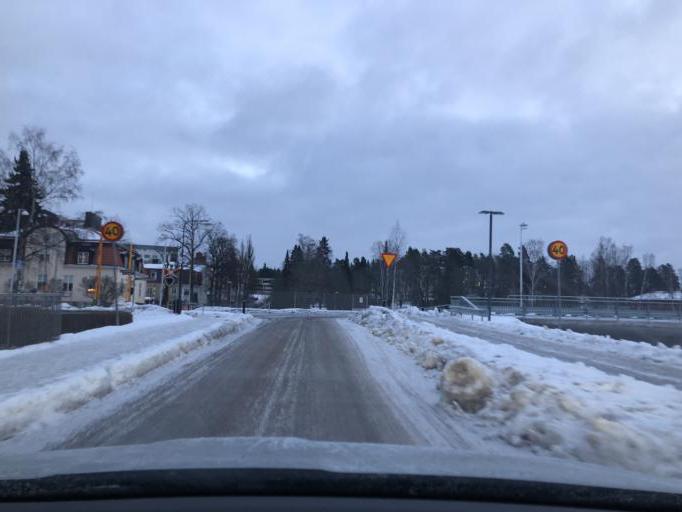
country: SE
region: Dalarna
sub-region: Faluns Kommun
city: Falun
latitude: 60.6053
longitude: 15.6385
